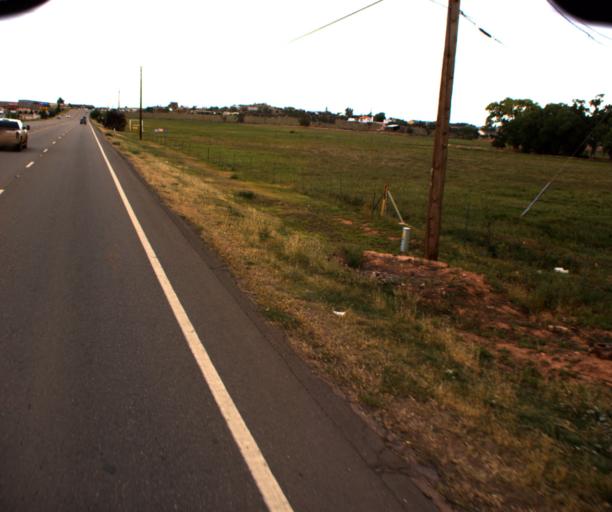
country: US
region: Arizona
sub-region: Navajo County
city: Taylor
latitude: 34.4858
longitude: -110.0830
